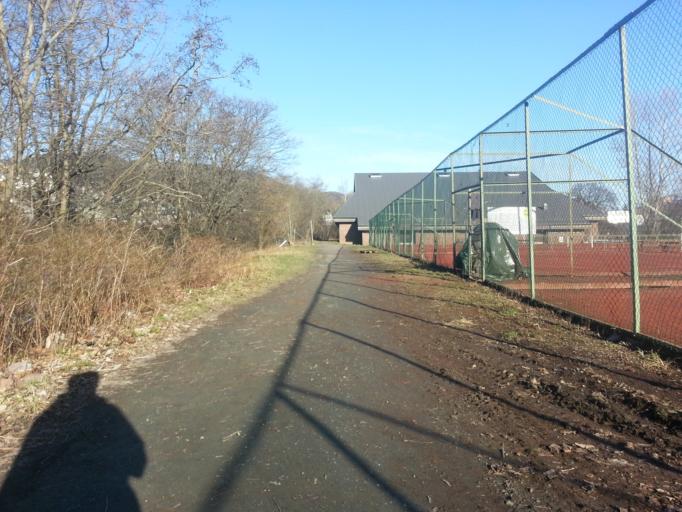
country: NO
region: Sor-Trondelag
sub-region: Trondheim
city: Trondheim
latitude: 63.4259
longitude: 10.3770
